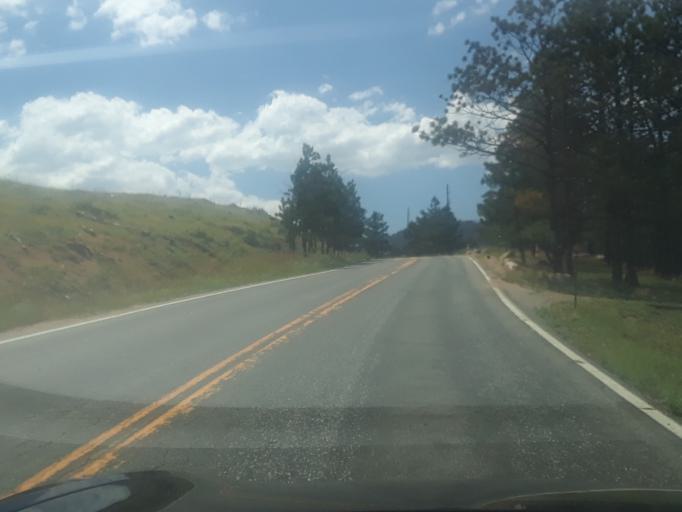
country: US
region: Colorado
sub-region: Boulder County
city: Boulder
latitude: 40.0536
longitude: -105.3563
